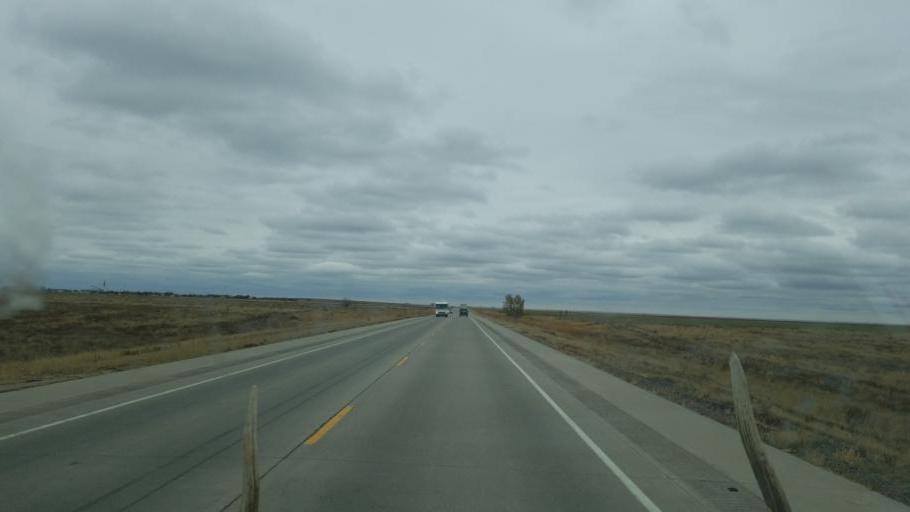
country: US
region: Colorado
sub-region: Kiowa County
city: Eads
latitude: 38.7425
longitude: -102.7766
